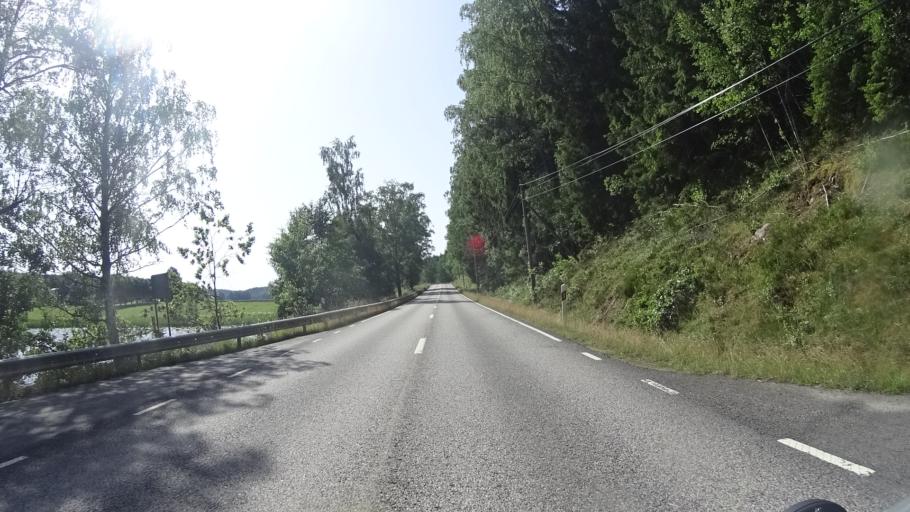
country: SE
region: Kalmar
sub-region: Vasterviks Kommun
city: Overum
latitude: 58.0055
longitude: 16.2712
